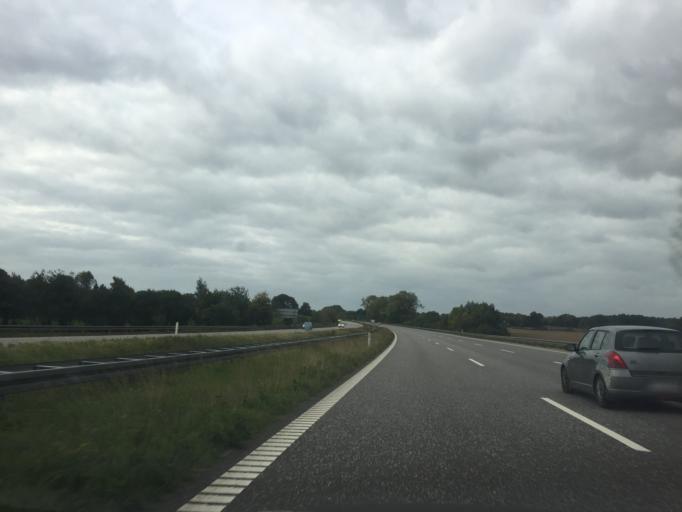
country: DK
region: Zealand
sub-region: Faxe Kommune
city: Ronnede
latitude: 55.2581
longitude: 11.9943
